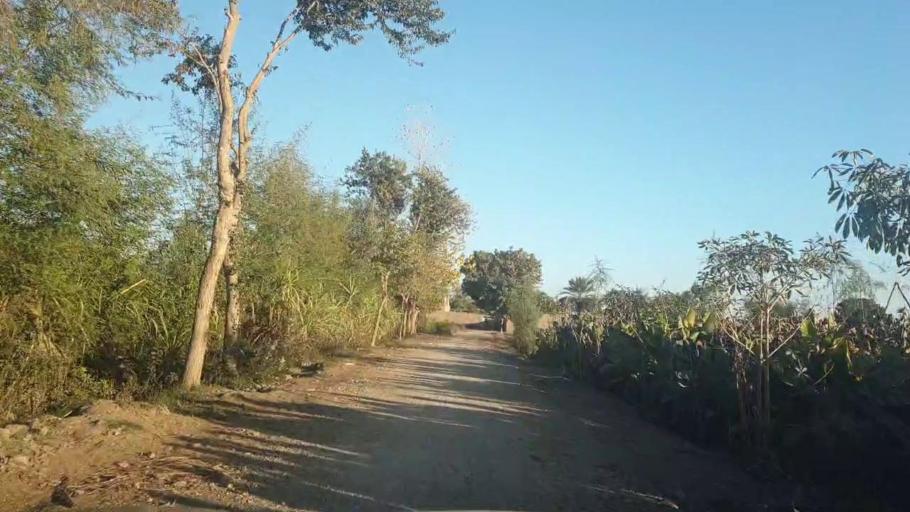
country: PK
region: Sindh
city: Ghotki
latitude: 28.0064
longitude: 69.2701
